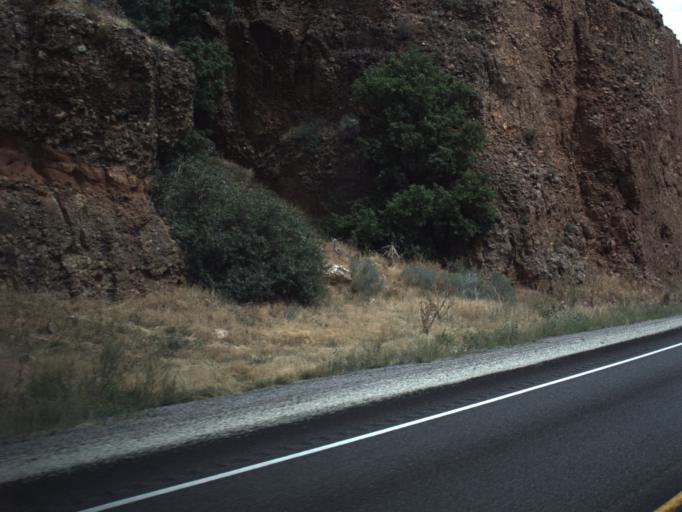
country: US
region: Utah
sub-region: Utah County
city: Mapleton
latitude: 39.9921
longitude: -111.3963
